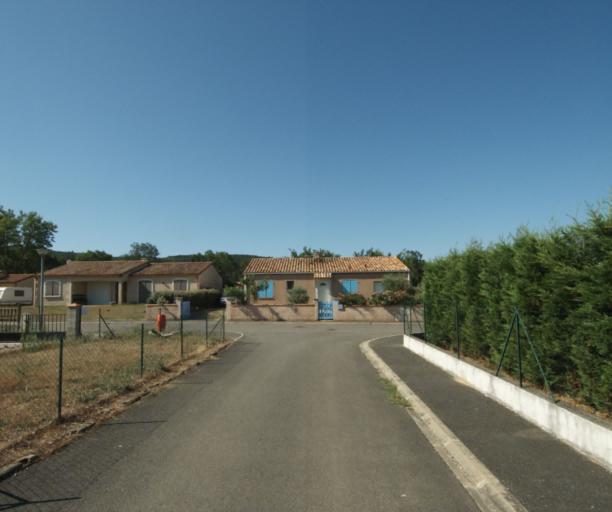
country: FR
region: Midi-Pyrenees
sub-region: Departement du Tarn
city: Soreze
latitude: 43.4524
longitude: 2.0395
